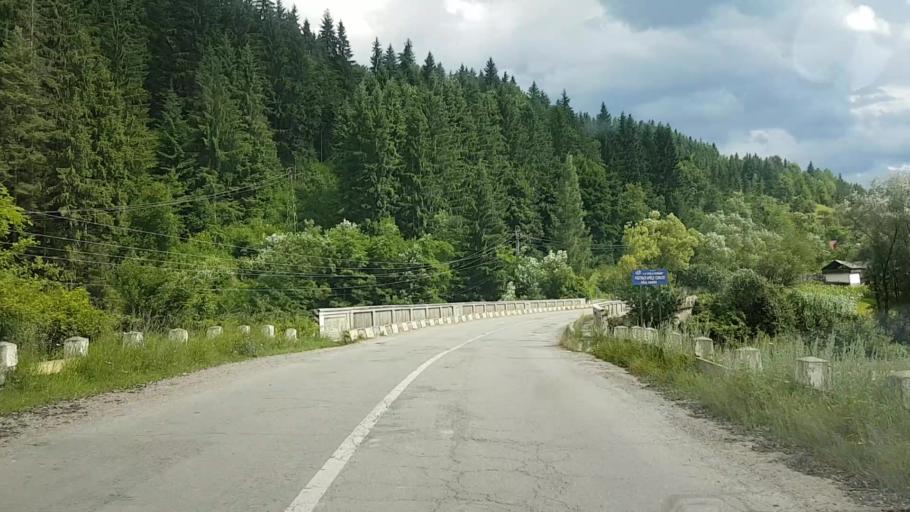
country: RO
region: Neamt
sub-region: Comuna Hangu
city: Hangu
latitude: 47.0593
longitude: 26.0365
